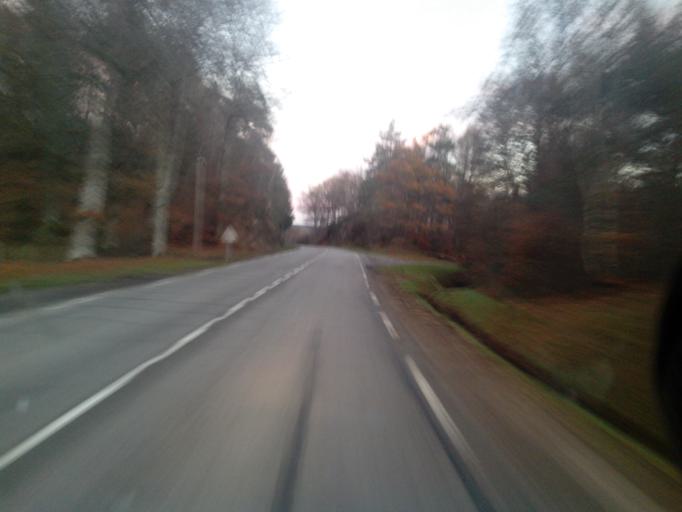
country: FR
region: Limousin
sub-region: Departement de la Correze
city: Meymac
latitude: 45.5129
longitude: 2.1858
